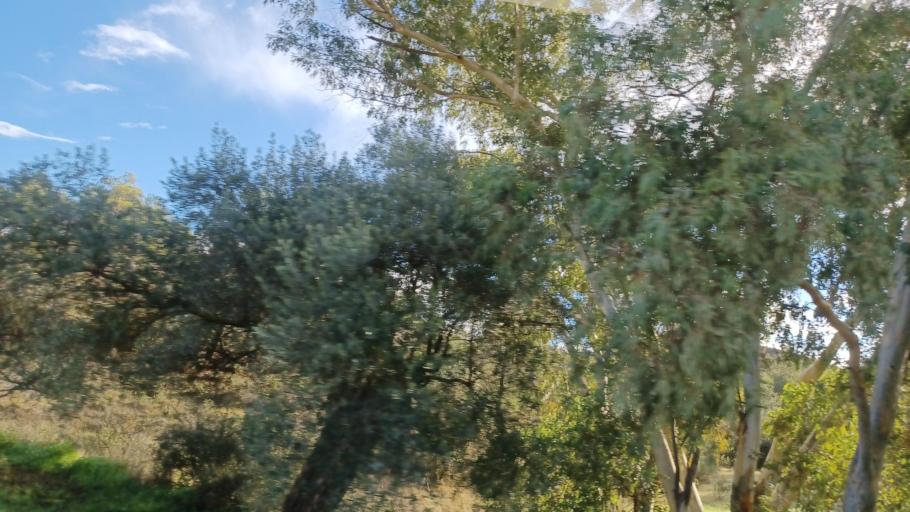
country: CY
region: Lefkosia
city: Lythrodontas
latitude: 34.9370
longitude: 33.2983
